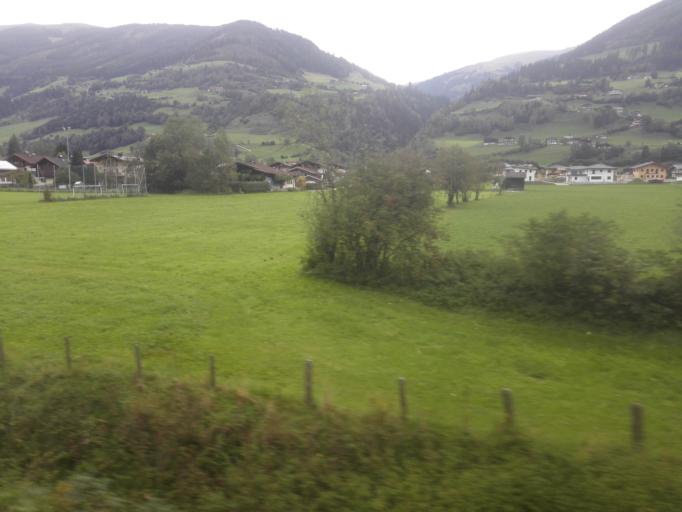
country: AT
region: Salzburg
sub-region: Politischer Bezirk Zell am See
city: Bramberg am Wildkogel
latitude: 47.2743
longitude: 12.3804
